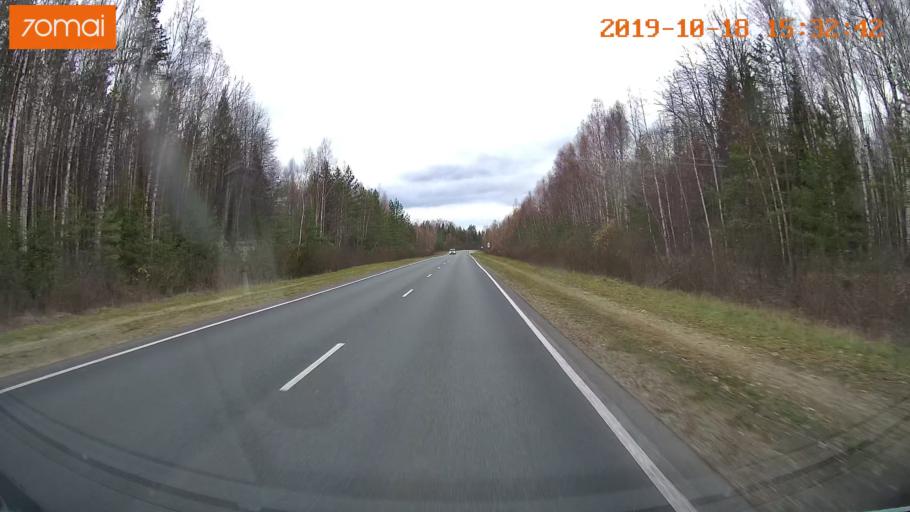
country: RU
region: Vladimir
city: Anopino
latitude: 55.8298
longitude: 40.6487
